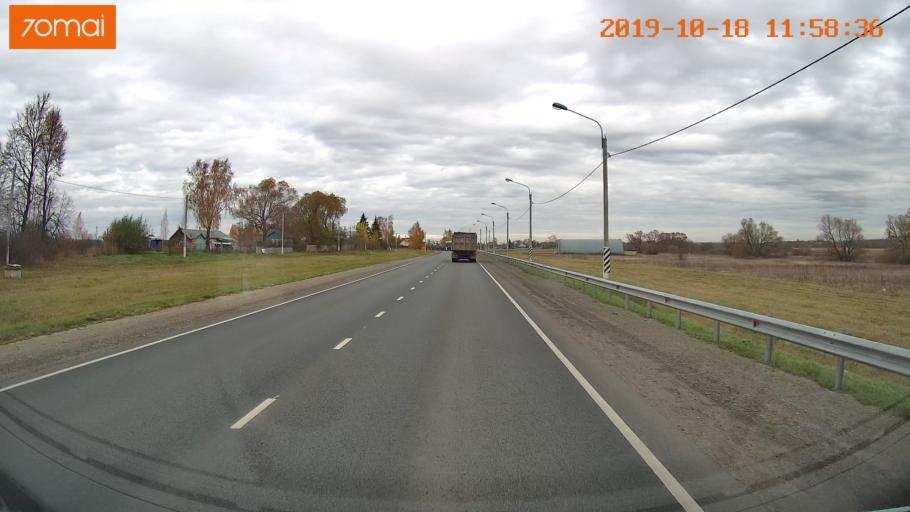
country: RU
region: Rjazan
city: Zakharovo
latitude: 54.2736
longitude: 39.1685
